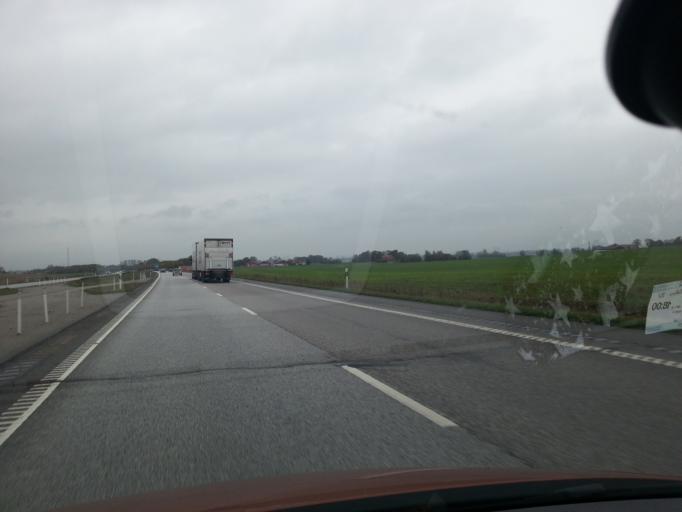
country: SE
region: Skane
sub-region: Burlovs Kommun
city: Arloev
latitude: 55.5948
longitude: 13.1172
